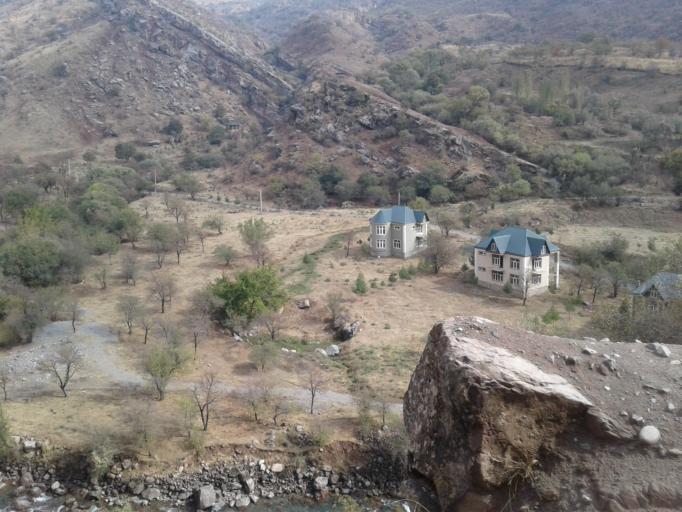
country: TJ
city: Shahrinav
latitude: 38.6999
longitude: 68.3680
